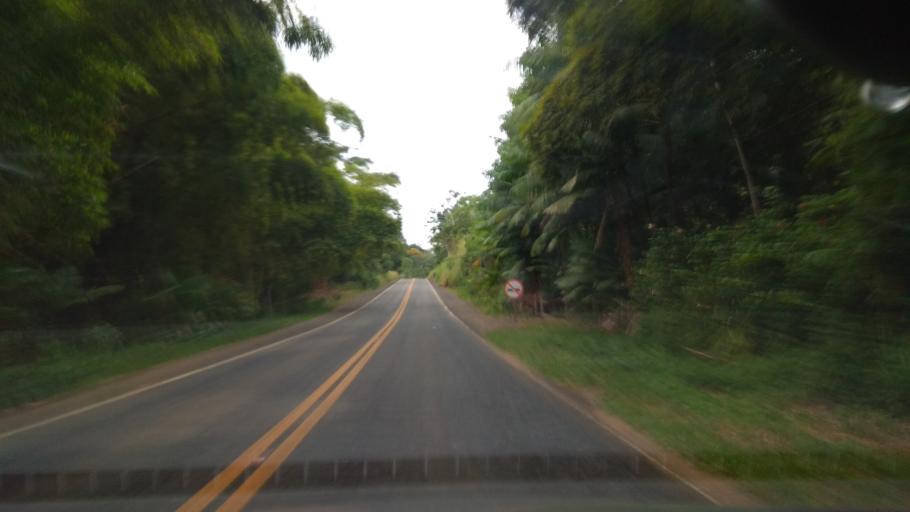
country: BR
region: Bahia
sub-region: Ibirapitanga
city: Ibirapitanga
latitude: -14.2306
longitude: -39.4342
